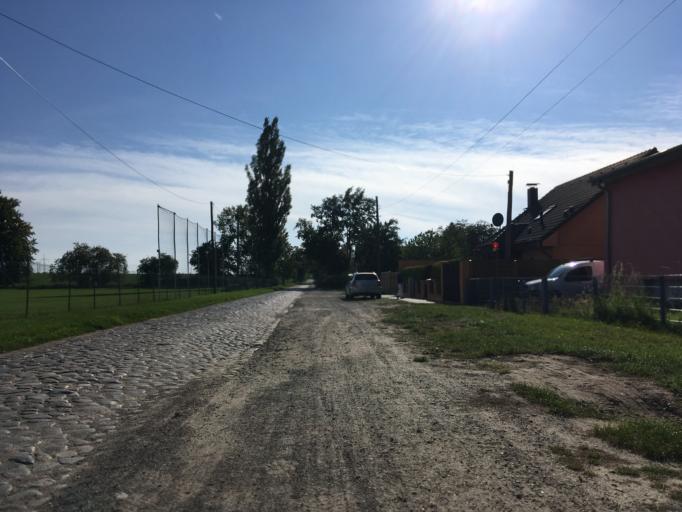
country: DE
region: Brandenburg
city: Altlandsberg
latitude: 52.5580
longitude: 13.7289
